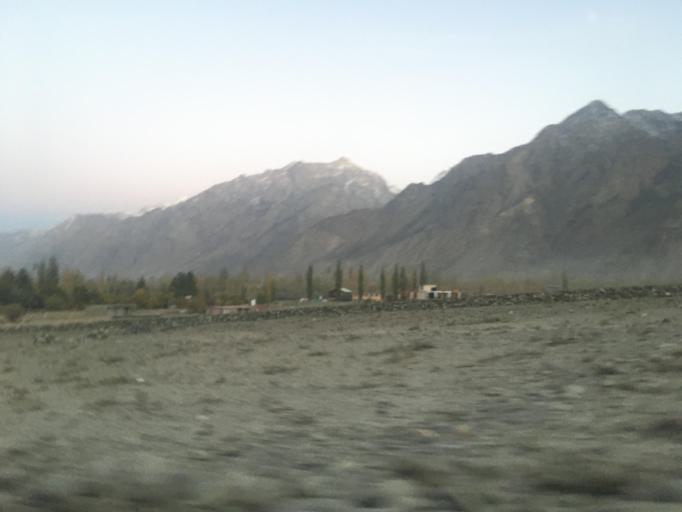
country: PK
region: Gilgit-Baltistan
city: Skardu
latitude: 35.2932
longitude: 75.5695
